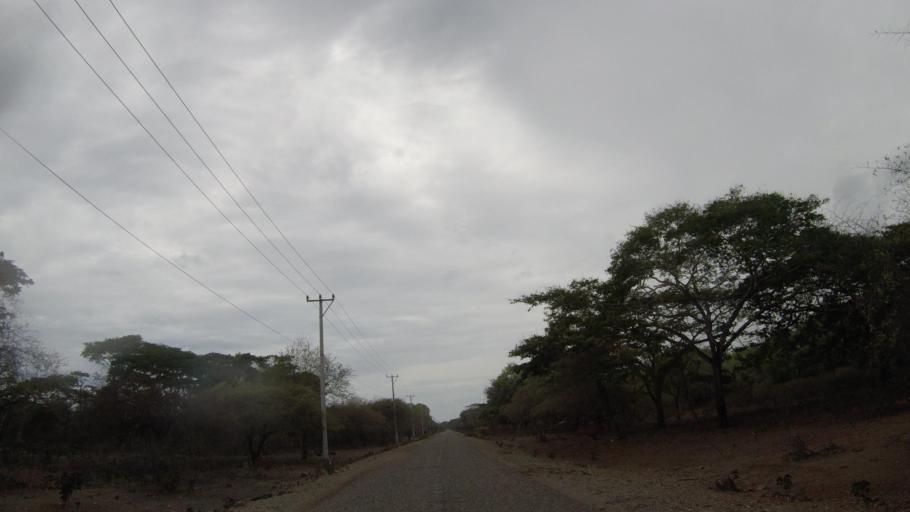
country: TL
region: Lautem
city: Lospalos
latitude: -8.3267
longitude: 126.9851
